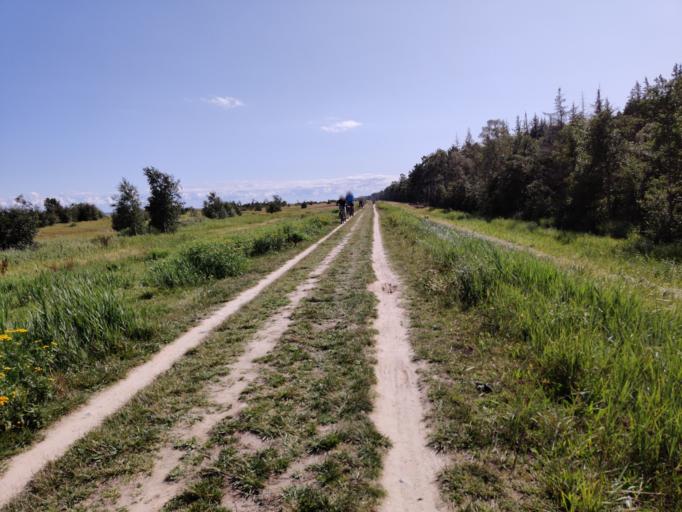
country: DK
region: Zealand
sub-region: Guldborgsund Kommune
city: Nykobing Falster
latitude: 54.6361
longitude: 11.9612
